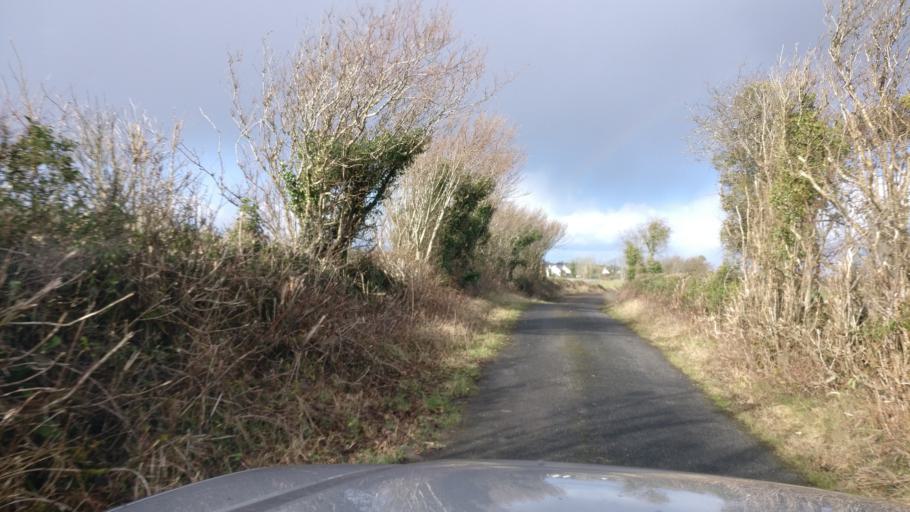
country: IE
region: Connaught
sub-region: County Galway
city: Oranmore
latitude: 53.2406
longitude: -8.8324
